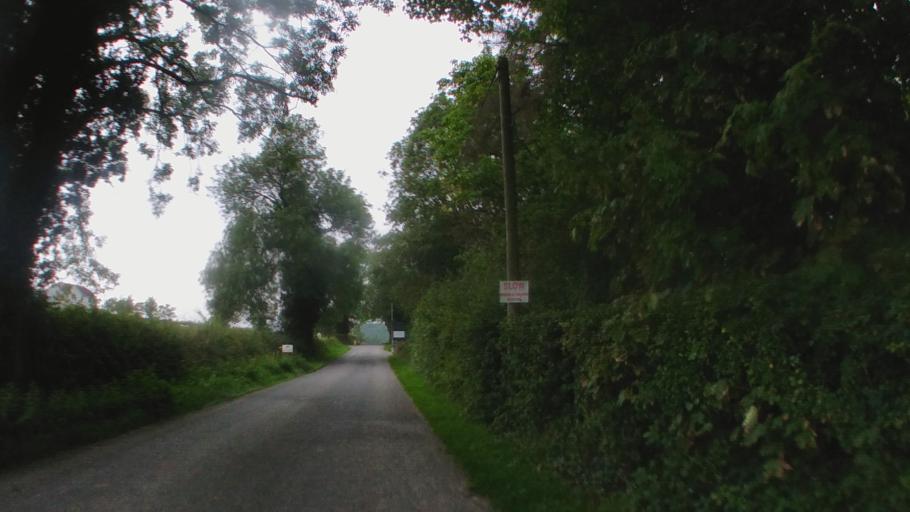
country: IE
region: Leinster
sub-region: Kilkenny
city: Kilkenny
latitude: 52.7083
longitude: -7.1942
